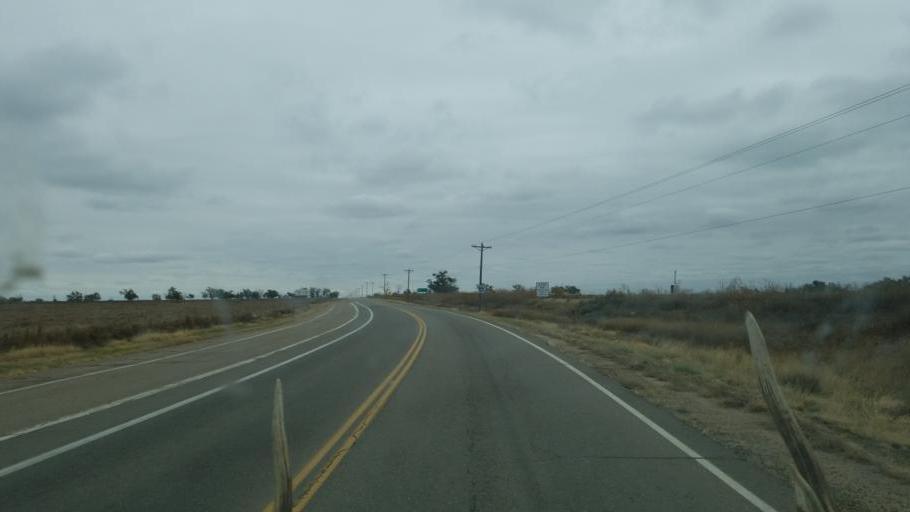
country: US
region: Colorado
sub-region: Crowley County
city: Ordway
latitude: 38.2177
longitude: -103.7469
